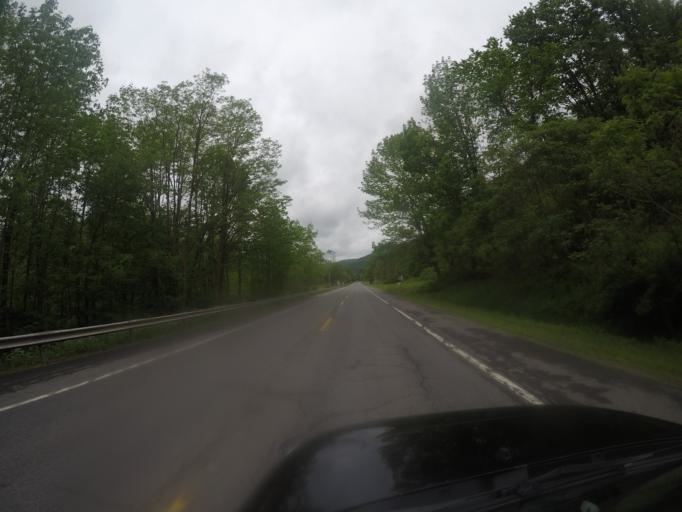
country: US
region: New York
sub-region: Ulster County
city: Shokan
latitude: 42.1181
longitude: -74.3802
